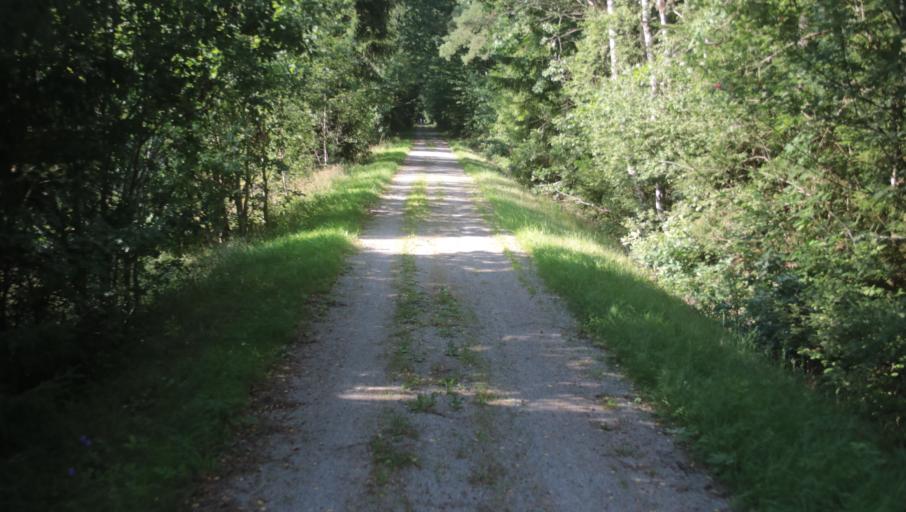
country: SE
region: Blekinge
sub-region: Karlshamns Kommun
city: Svangsta
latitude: 56.3433
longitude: 14.6959
